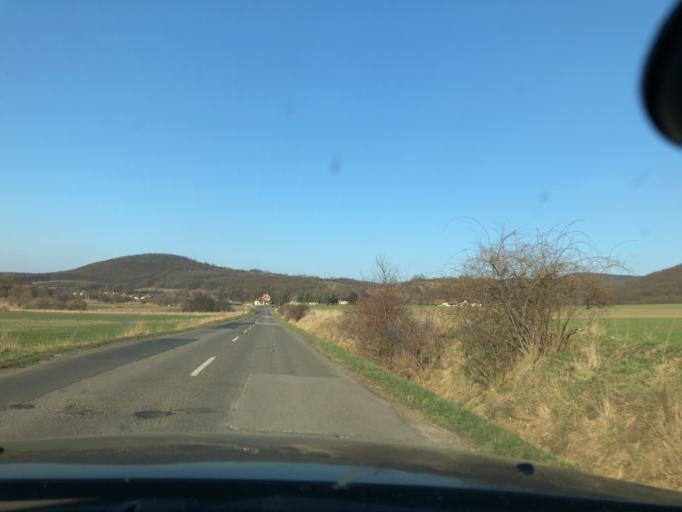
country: HU
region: Nograd
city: Bujak
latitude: 47.9627
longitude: 19.6031
